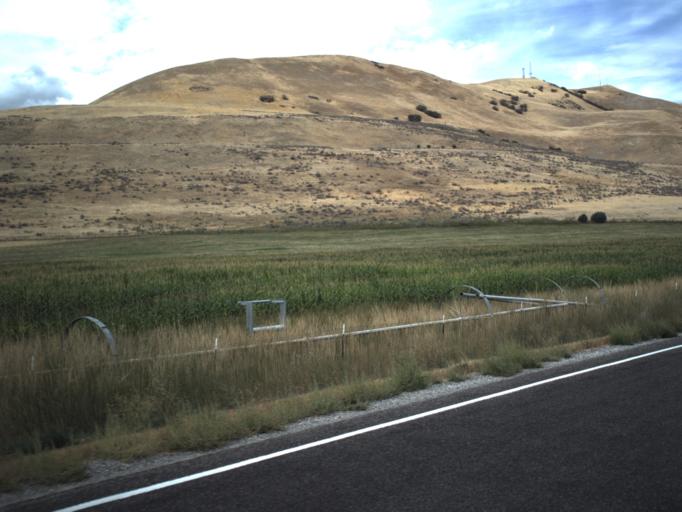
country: US
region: Utah
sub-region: Cache County
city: Benson
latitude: 41.8821
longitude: -111.9517
